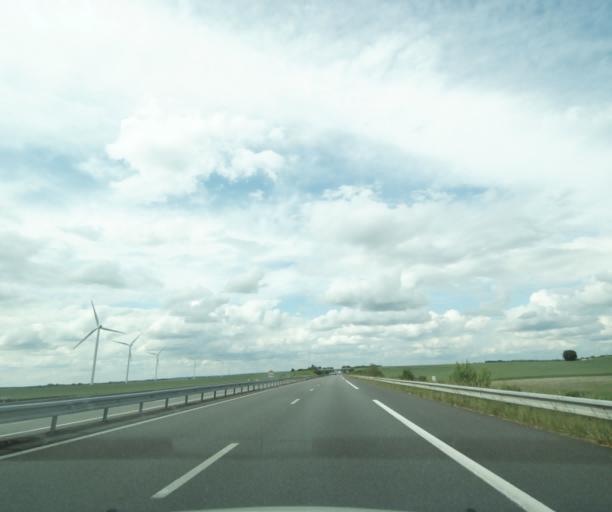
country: FR
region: Centre
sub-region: Departement du Cher
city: Mehun-sur-Yevre
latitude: 47.1336
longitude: 2.1878
